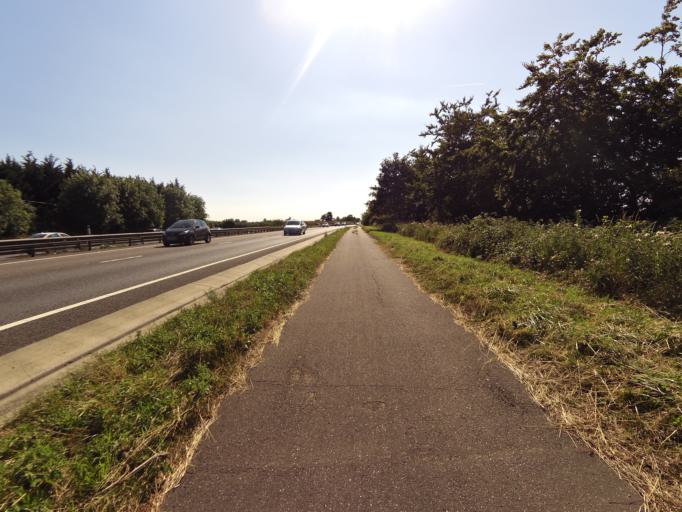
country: GB
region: England
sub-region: Essex
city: Marks Tey
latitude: 51.8666
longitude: 0.7610
